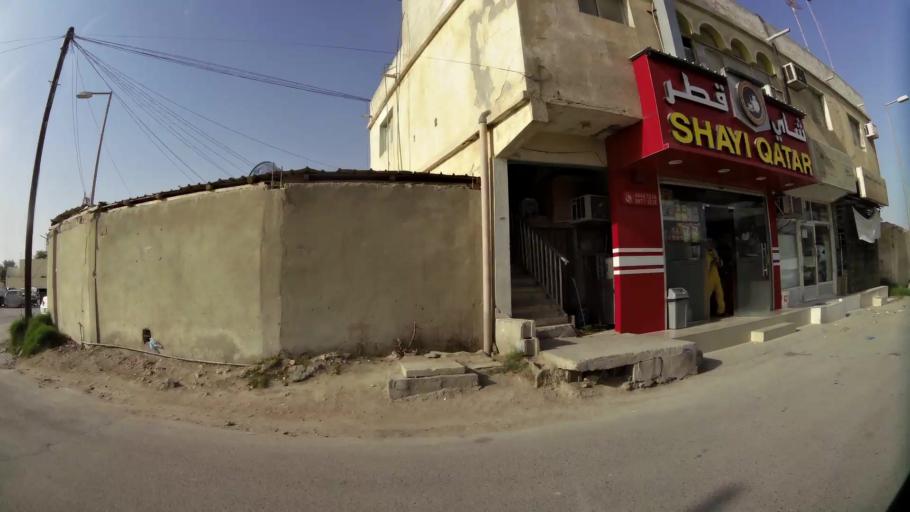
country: QA
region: Baladiyat ar Rayyan
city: Ar Rayyan
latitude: 25.3319
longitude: 51.4443
